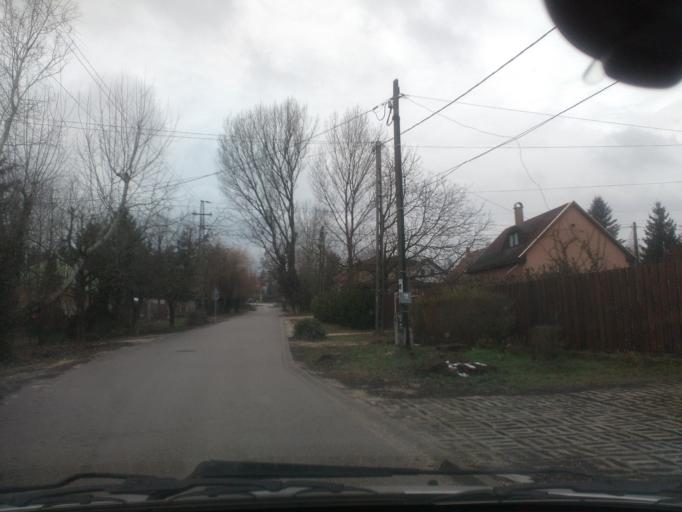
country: HU
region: Pest
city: Pilisvorosvar
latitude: 47.6085
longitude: 18.9176
